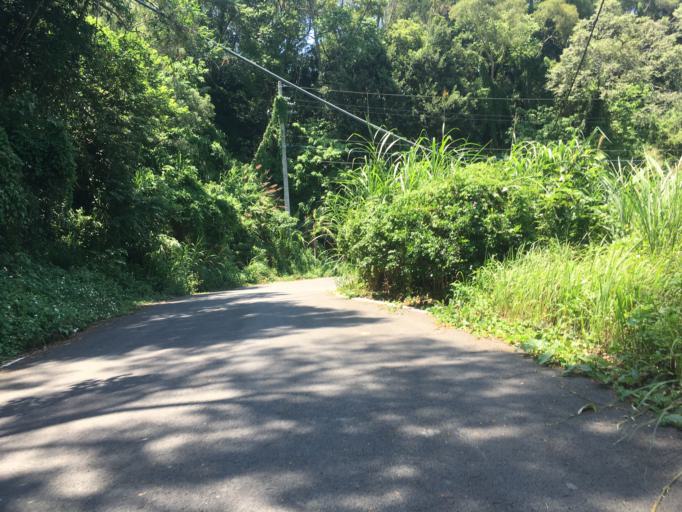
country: TW
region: Taiwan
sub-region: Hsinchu
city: Hsinchu
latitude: 24.7319
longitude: 120.9803
